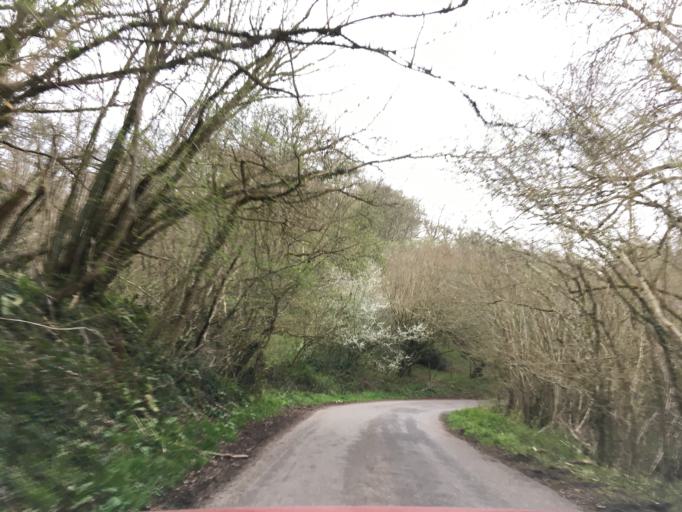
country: GB
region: England
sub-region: Gloucestershire
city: Wotton-under-Edge
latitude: 51.6002
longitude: -2.2978
